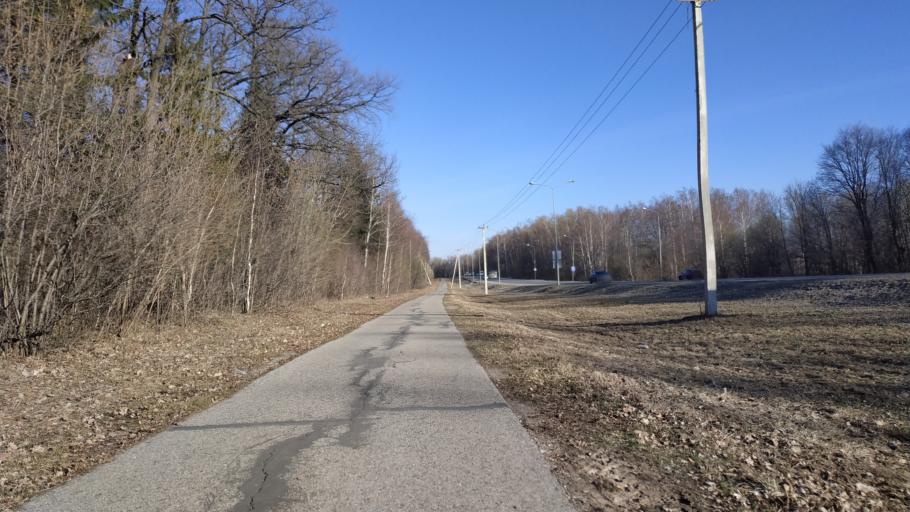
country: RU
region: Chuvashia
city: Novyye Lapsary
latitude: 56.1320
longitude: 47.1114
